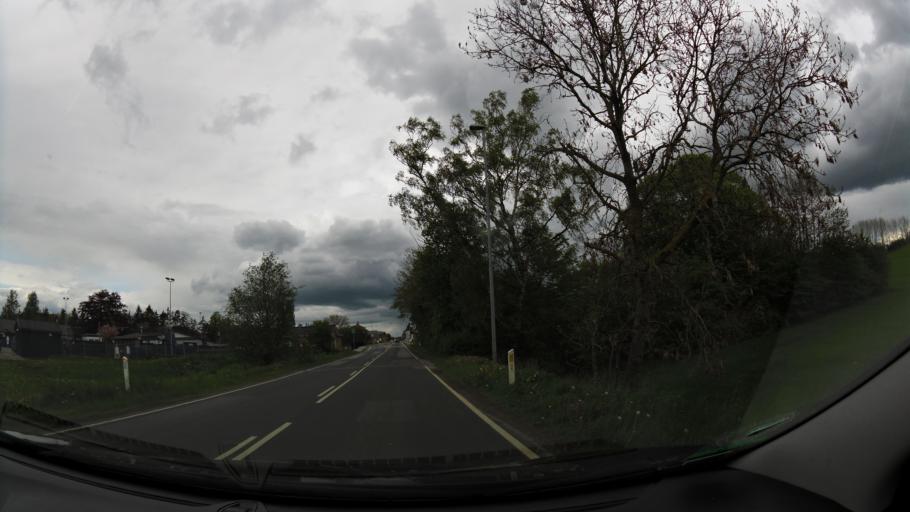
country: DK
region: South Denmark
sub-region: Svendborg Kommune
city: Thuro By
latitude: 55.1668
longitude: 10.7345
